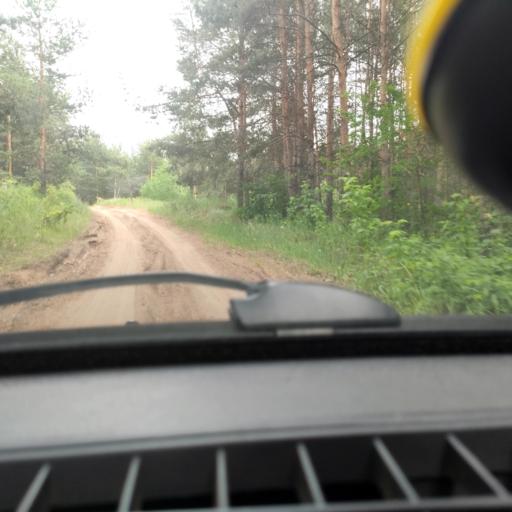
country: RU
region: Samara
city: Zhigulevsk
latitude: 53.5033
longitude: 49.5034
